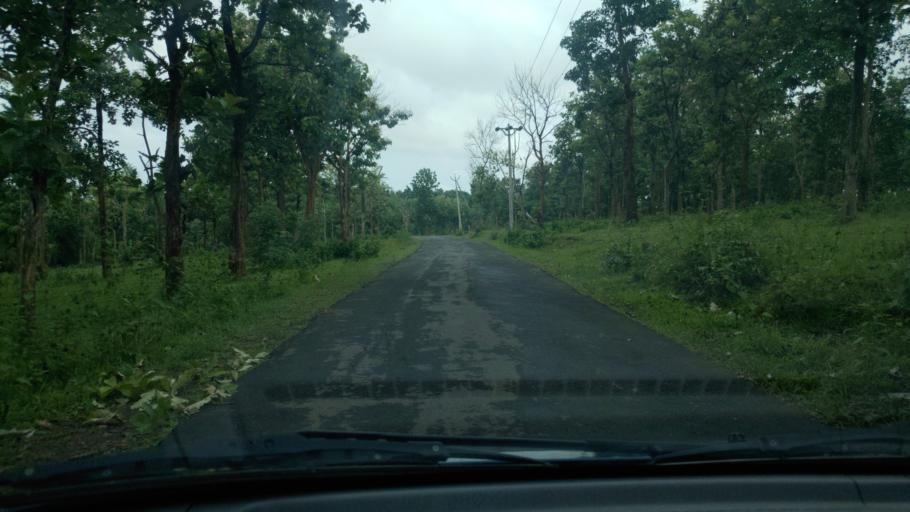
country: IN
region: Kerala
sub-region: Wayanad
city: Panamaram
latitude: 11.7095
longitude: 76.2757
